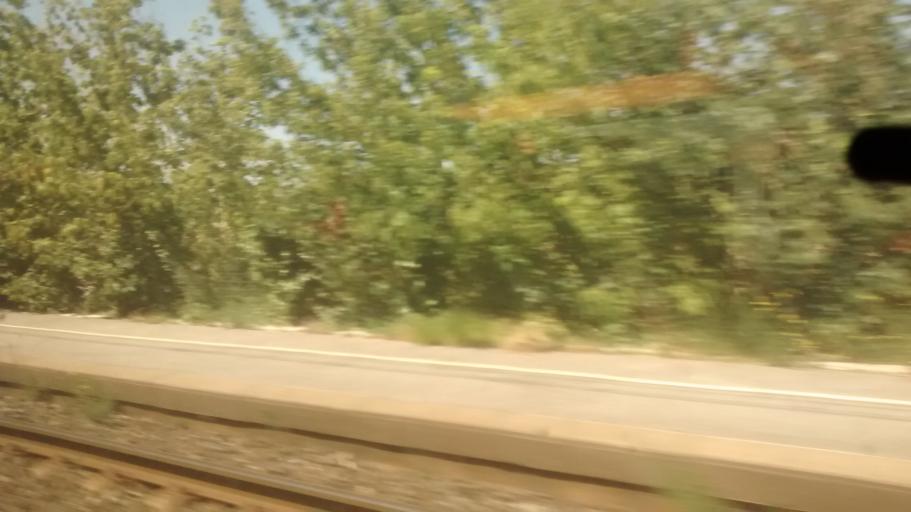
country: FR
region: Languedoc-Roussillon
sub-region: Departement du Gard
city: Manduel
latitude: 43.8266
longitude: 4.4786
